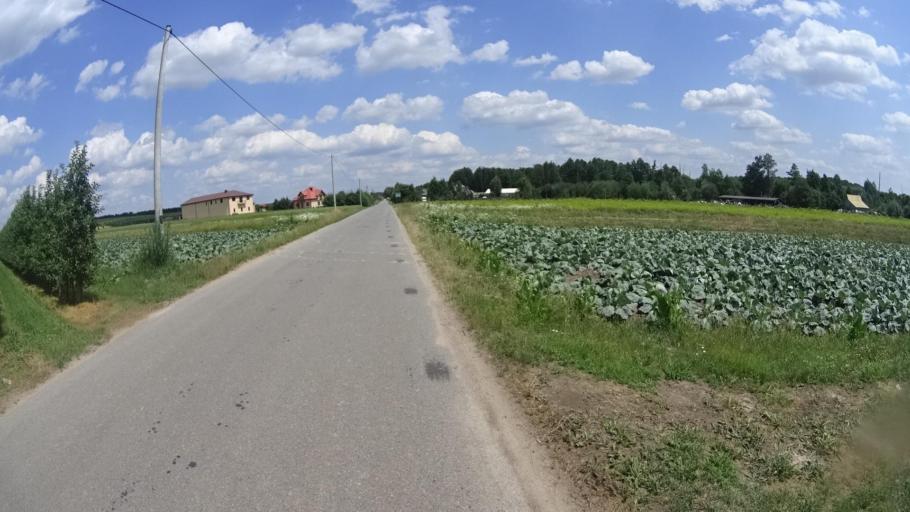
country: PL
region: Masovian Voivodeship
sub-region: Powiat grojecki
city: Goszczyn
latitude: 51.6900
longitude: 20.8597
